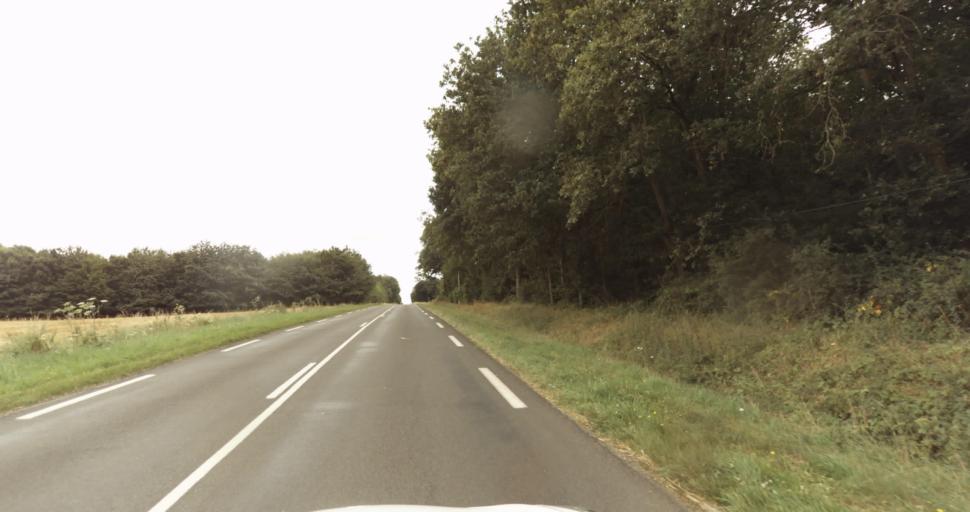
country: FR
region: Haute-Normandie
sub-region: Departement de l'Eure
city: La Madeleine-de-Nonancourt
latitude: 48.8117
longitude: 1.1879
